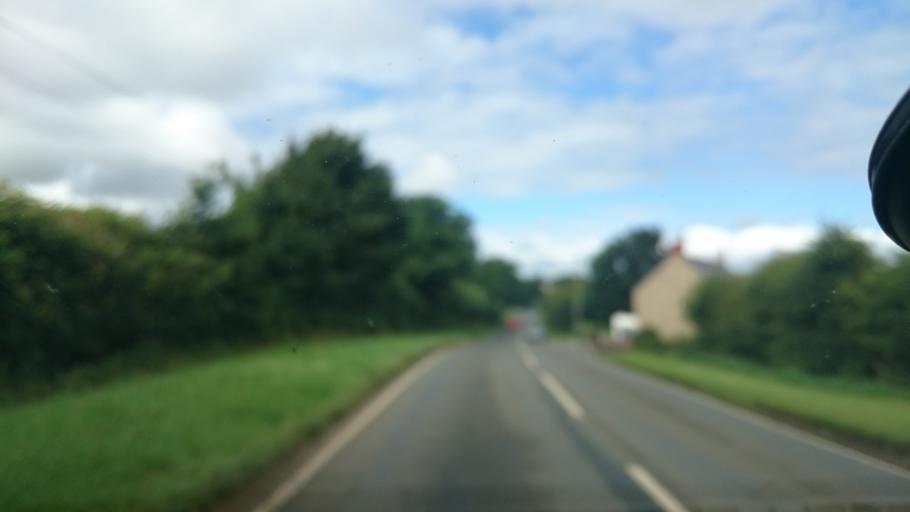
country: GB
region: Wales
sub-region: Pembrokeshire
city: Freystrop
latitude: 51.7562
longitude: -4.9558
